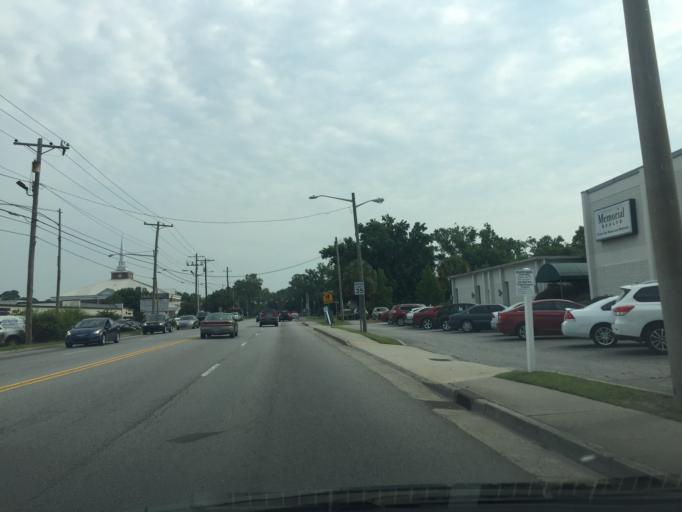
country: US
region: Georgia
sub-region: Chatham County
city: Thunderbolt
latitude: 32.0299
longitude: -81.0925
